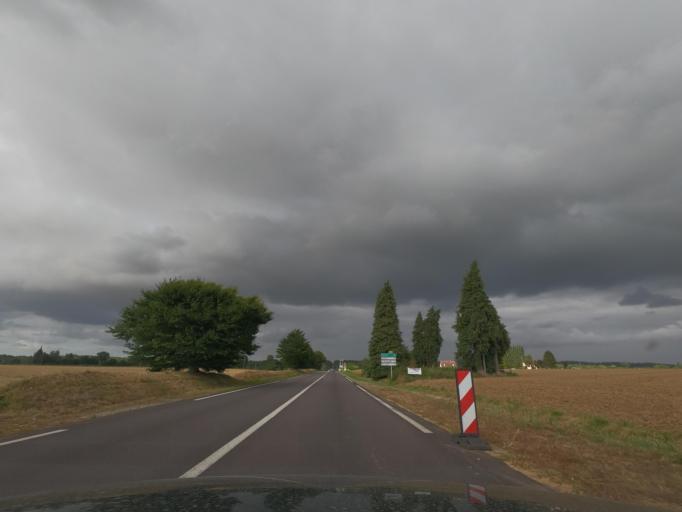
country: FR
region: Haute-Normandie
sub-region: Departement de l'Eure
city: Menneval
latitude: 49.1161
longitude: 0.6233
